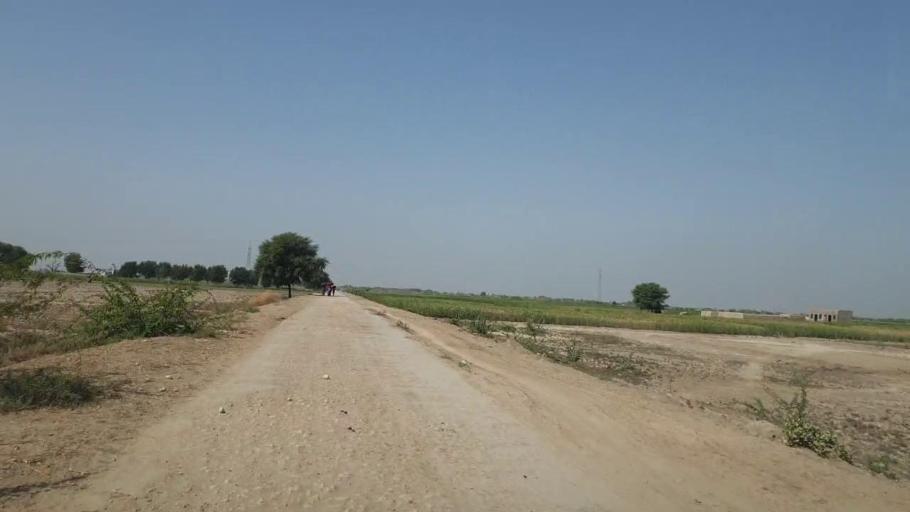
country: PK
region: Sindh
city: Naukot
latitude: 24.9745
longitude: 69.4777
